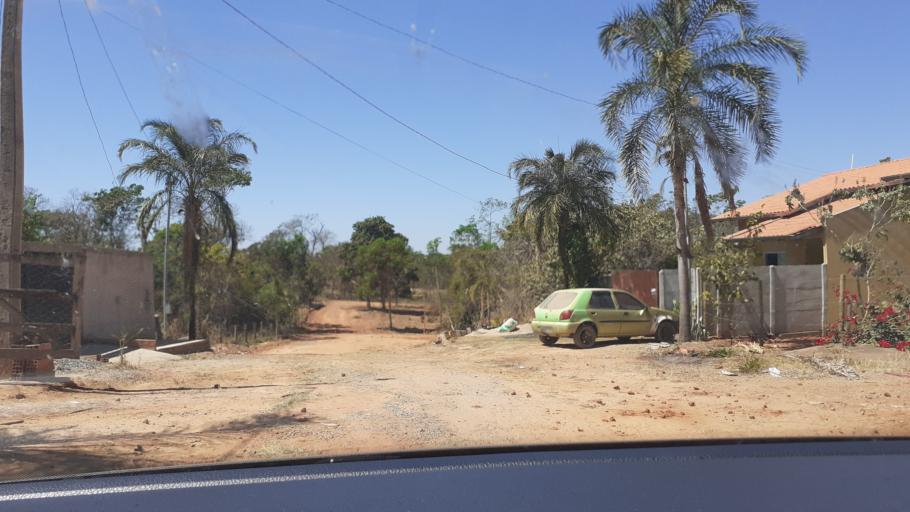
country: BR
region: Goias
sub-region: Caldas Novas
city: Caldas Novas
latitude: -17.7456
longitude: -48.6549
